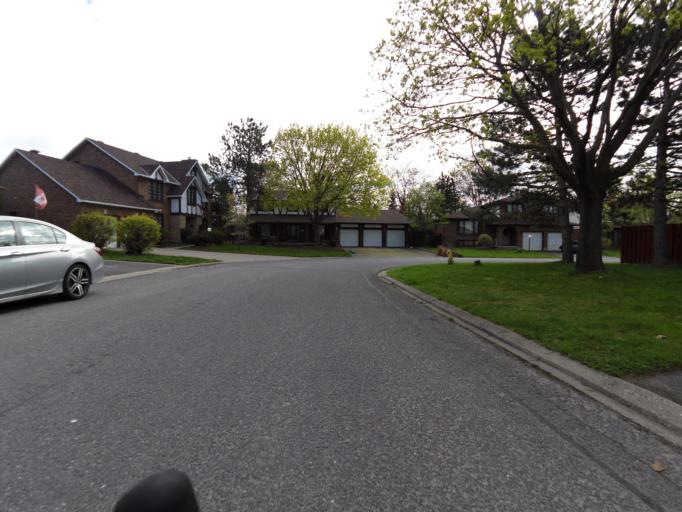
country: CA
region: Ontario
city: Bells Corners
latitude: 45.2925
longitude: -75.7447
